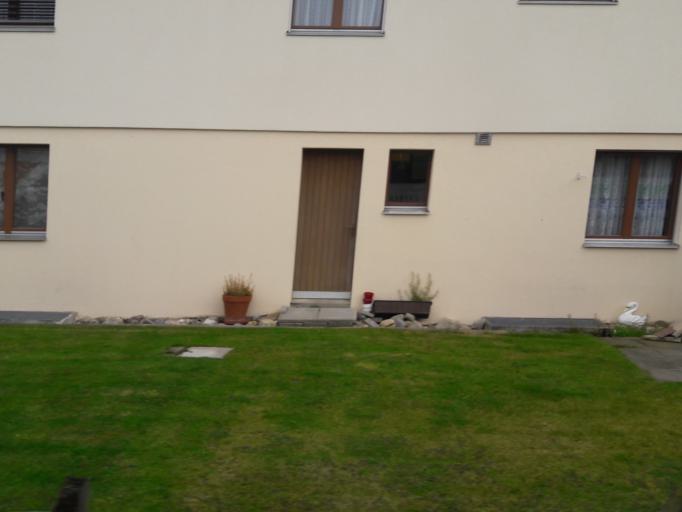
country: CH
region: Schwyz
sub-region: Bezirk Schwyz
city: Rothenthurm
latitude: 47.1094
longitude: 8.6771
